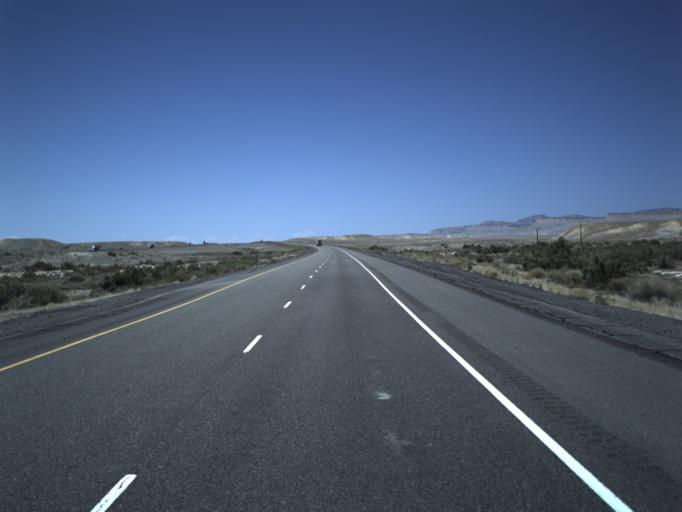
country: US
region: Utah
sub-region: Grand County
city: Moab
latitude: 38.9420
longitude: -109.5214
